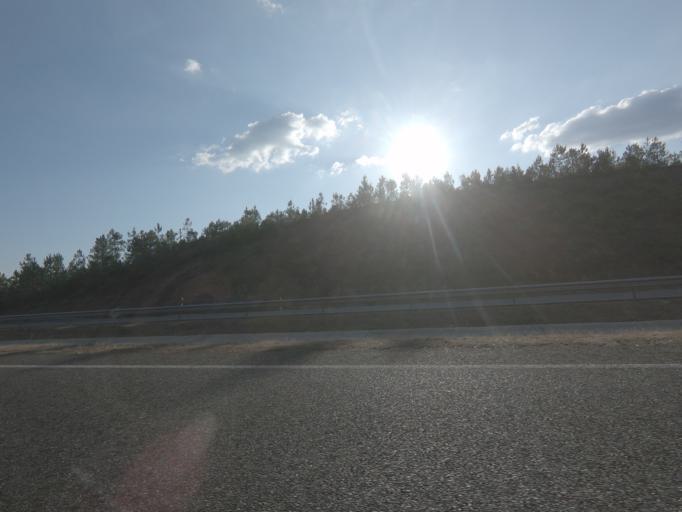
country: ES
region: Galicia
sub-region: Provincia de Ourense
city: Oimbra
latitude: 41.8857
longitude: -7.4268
